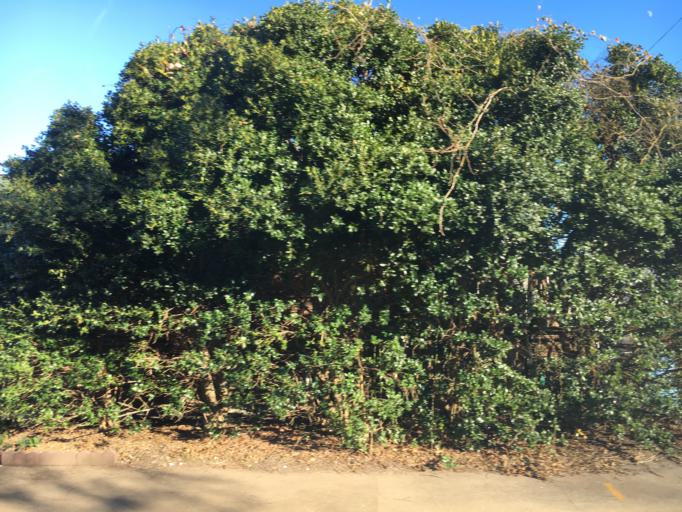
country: US
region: South Carolina
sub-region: Spartanburg County
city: Duncan
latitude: 34.9379
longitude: -82.1449
